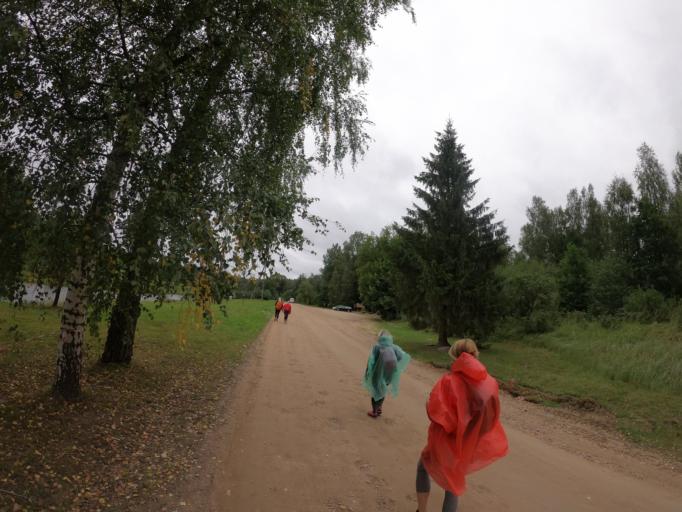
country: LV
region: Kuldigas Rajons
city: Kuldiga
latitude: 57.0064
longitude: 21.9779
